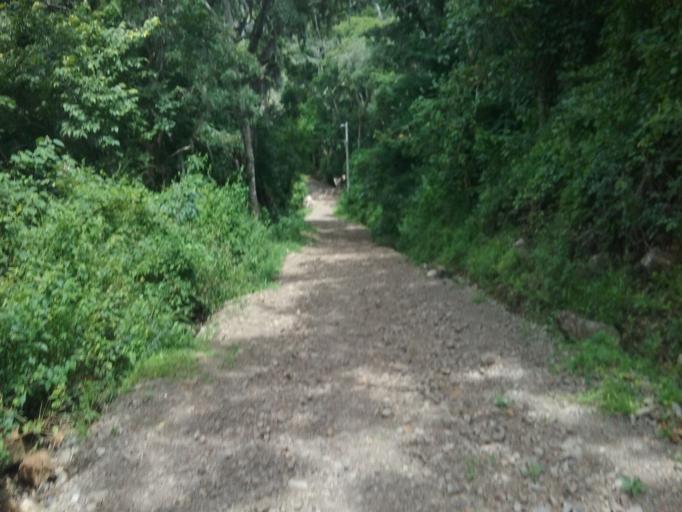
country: NI
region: Matagalpa
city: Matagalpa
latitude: 12.8692
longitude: -85.9175
